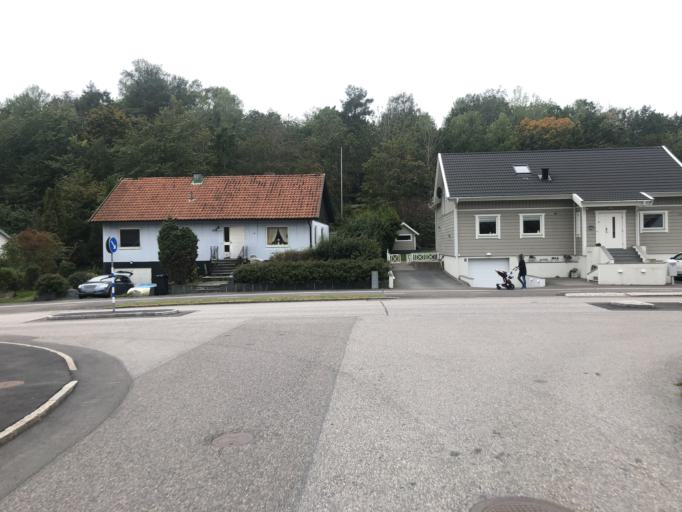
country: SE
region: Vaestra Goetaland
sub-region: Molndal
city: Moelndal
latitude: 57.6626
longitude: 12.0277
